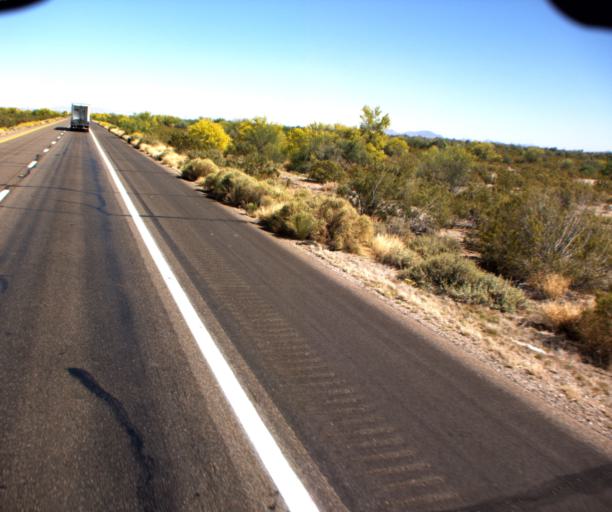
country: US
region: Arizona
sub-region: Pinal County
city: Maricopa
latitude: 32.8298
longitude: -112.0198
